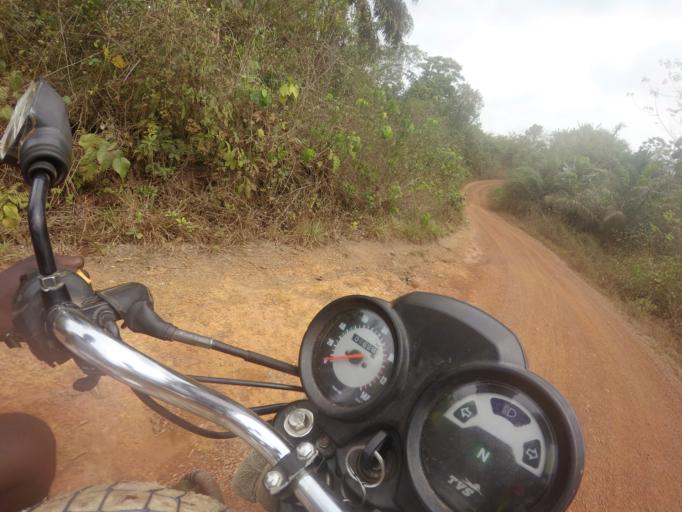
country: SL
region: Southern Province
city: Zimmi
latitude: 7.2053
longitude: -11.2094
